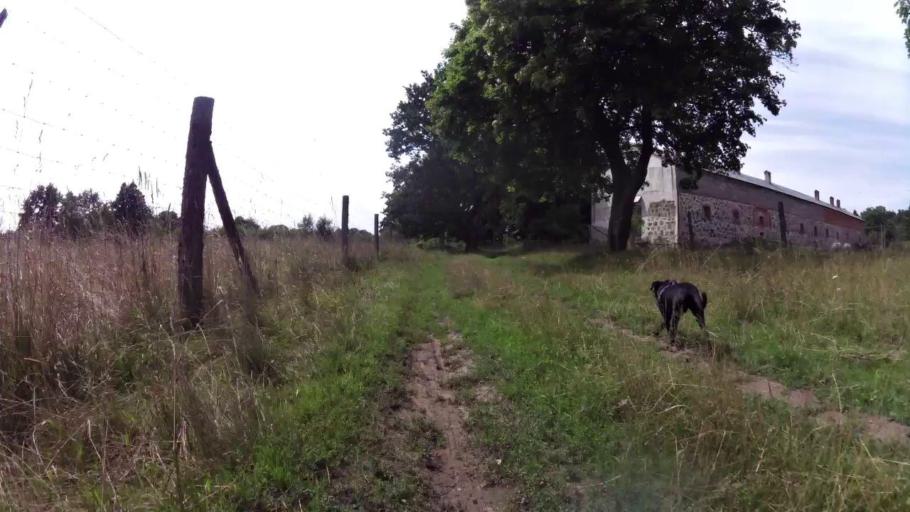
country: PL
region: West Pomeranian Voivodeship
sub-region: Powiat lobeski
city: Wegorzyno
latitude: 53.5147
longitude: 15.6551
